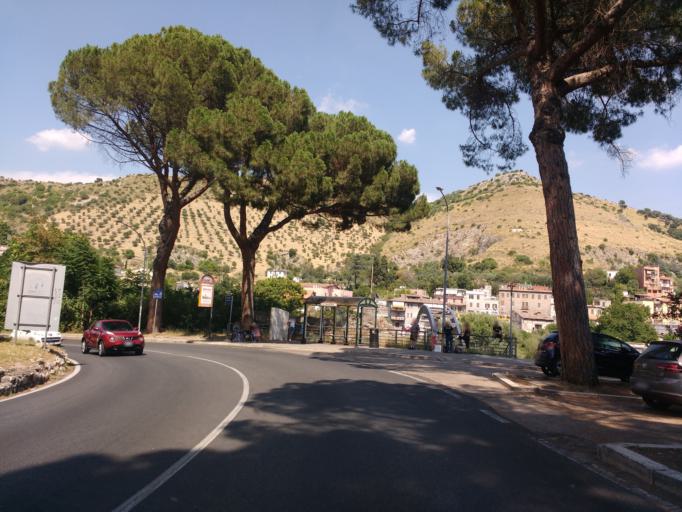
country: IT
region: Latium
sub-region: Citta metropolitana di Roma Capitale
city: Tivoli
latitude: 41.9598
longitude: 12.8030
